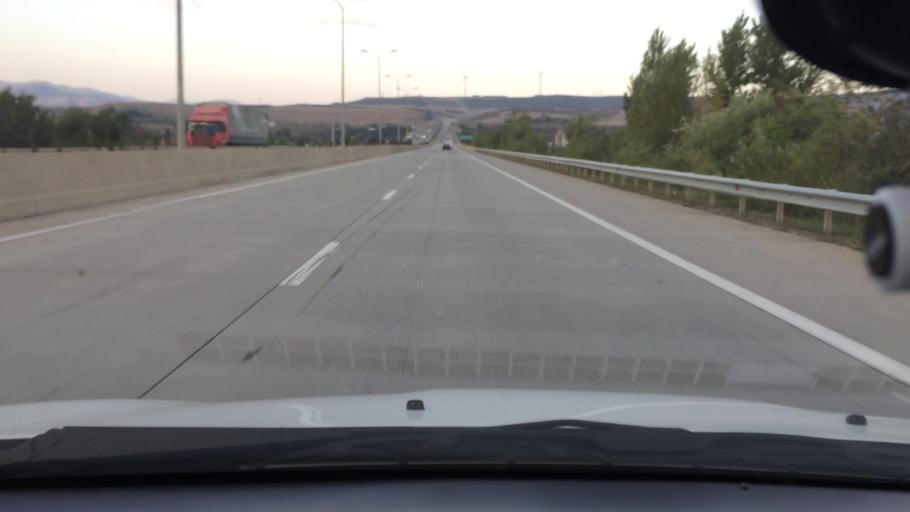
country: GE
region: Shida Kartli
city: Gori
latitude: 42.0177
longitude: 44.0949
